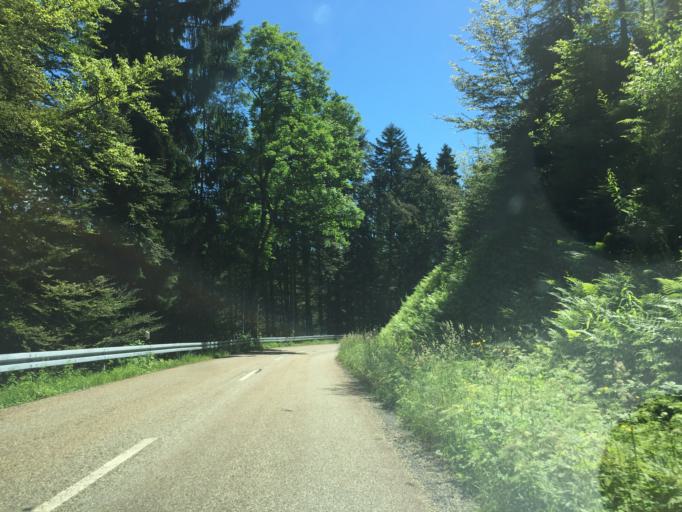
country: DE
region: Baden-Wuerttemberg
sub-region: Freiburg Region
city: Schonenberg
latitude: 47.8102
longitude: 7.8773
